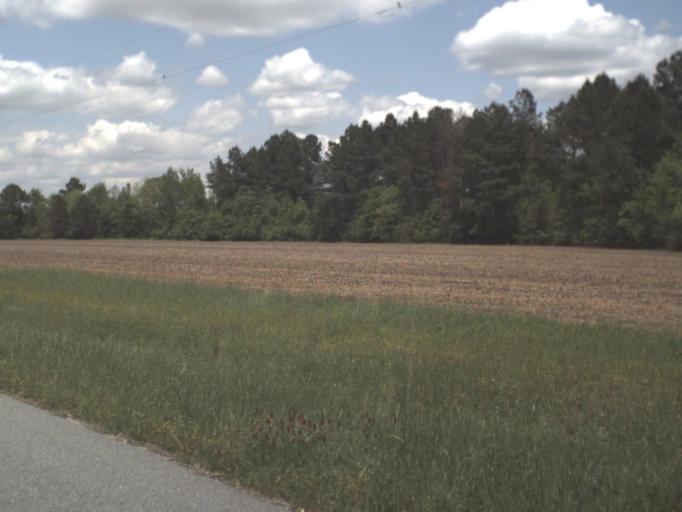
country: US
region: Alabama
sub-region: Escambia County
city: Atmore
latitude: 30.8542
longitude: -87.4402
